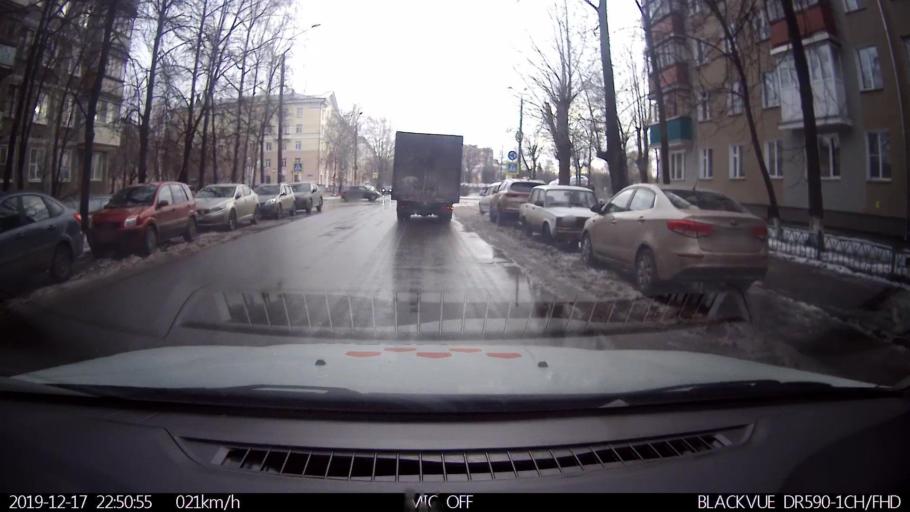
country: RU
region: Nizjnij Novgorod
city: Neklyudovo
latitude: 56.3462
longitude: 43.8628
